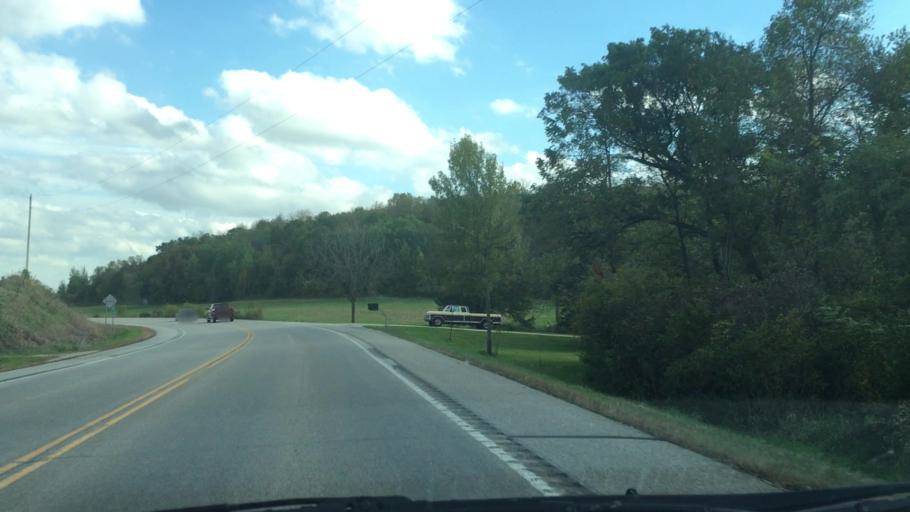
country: US
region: Minnesota
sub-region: Fillmore County
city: Chatfield
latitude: 43.8057
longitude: -92.1342
